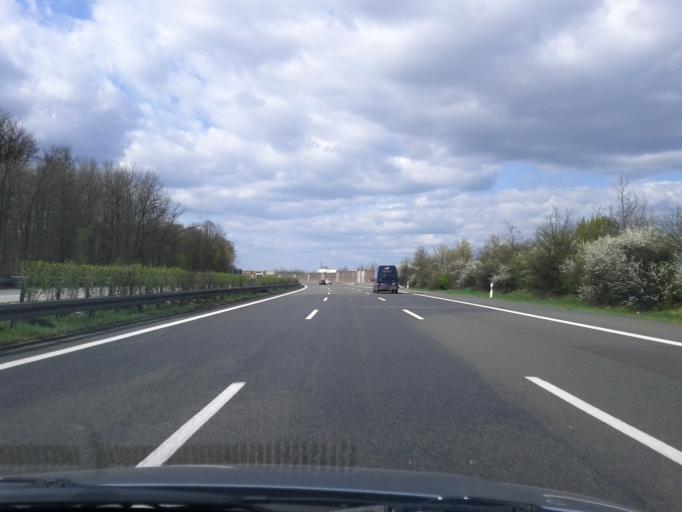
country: DE
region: Brandenburg
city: Woltersdorf
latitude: 52.4564
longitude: 13.7983
